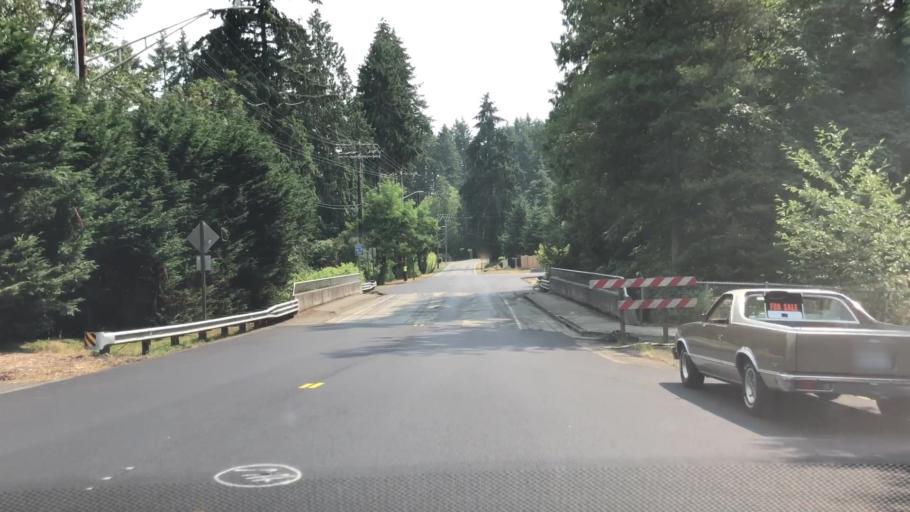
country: US
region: Washington
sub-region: Snohomish County
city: Brier
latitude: 47.7992
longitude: -122.2548
